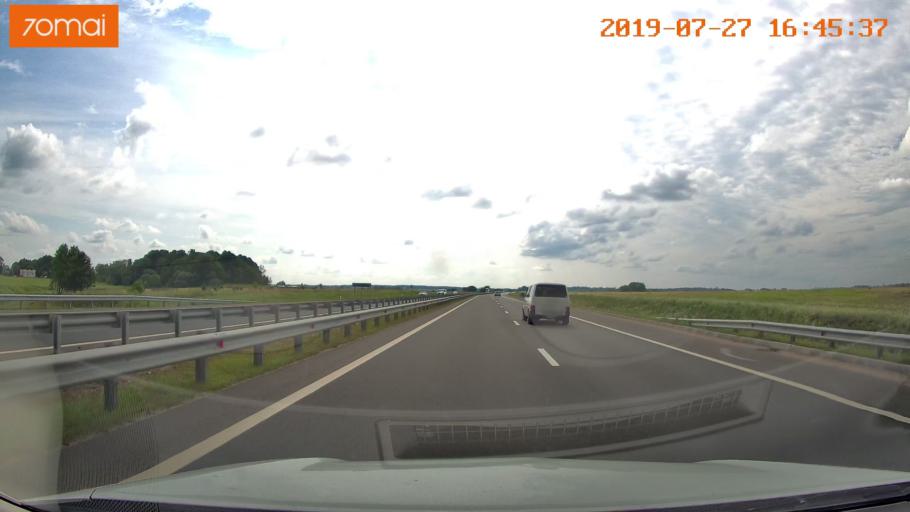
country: RU
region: Kaliningrad
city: Gvardeysk
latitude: 54.6690
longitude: 21.0444
